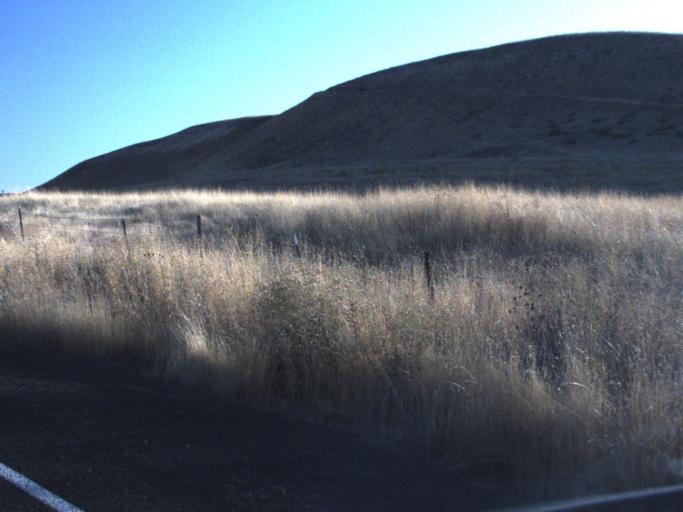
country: US
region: Washington
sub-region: Walla Walla County
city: Waitsburg
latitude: 46.6415
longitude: -118.2450
